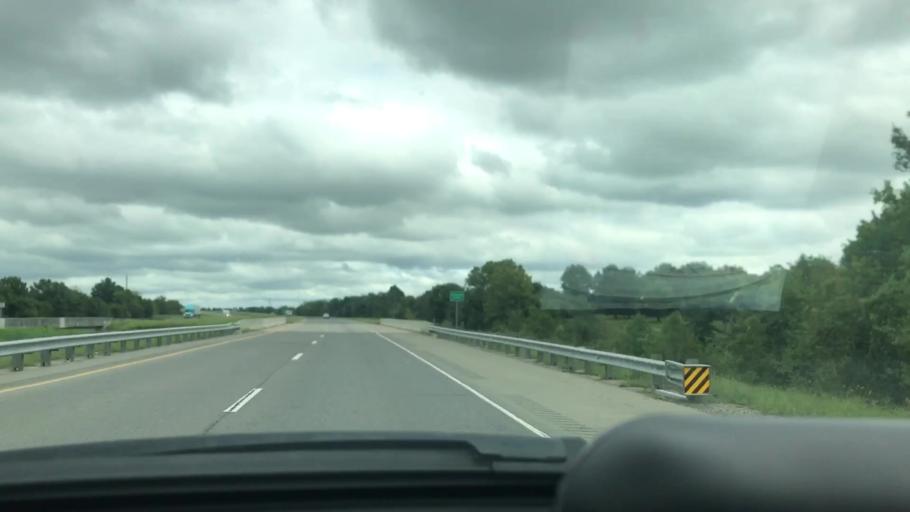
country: US
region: Oklahoma
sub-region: McIntosh County
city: Checotah
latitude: 35.5627
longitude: -95.4929
